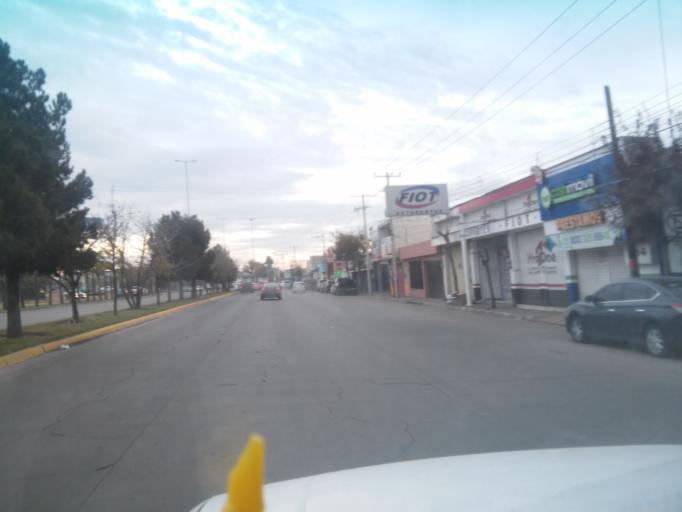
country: MX
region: Durango
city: Victoria de Durango
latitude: 24.0040
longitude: -104.6549
